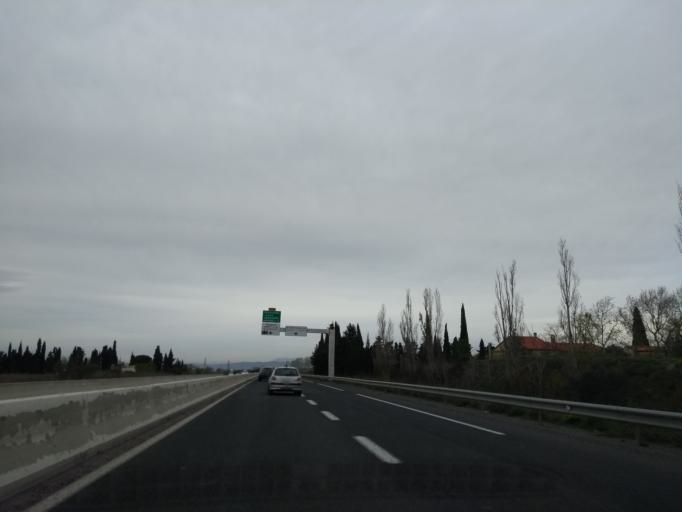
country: FR
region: Languedoc-Roussillon
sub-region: Departement des Pyrenees-Orientales
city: Toulouges
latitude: 42.6728
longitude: 2.8566
